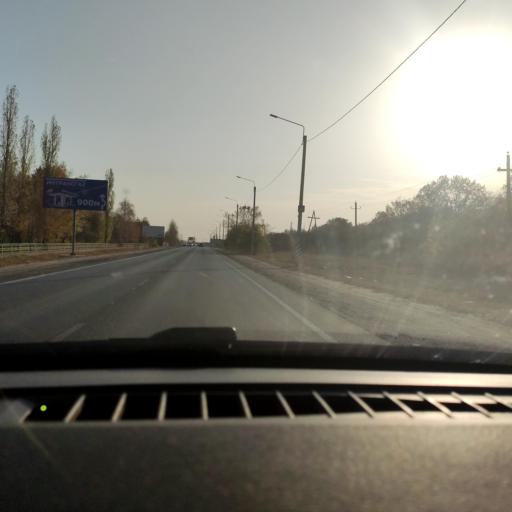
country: RU
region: Voronezj
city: Semiluki
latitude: 51.7296
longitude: 39.0382
